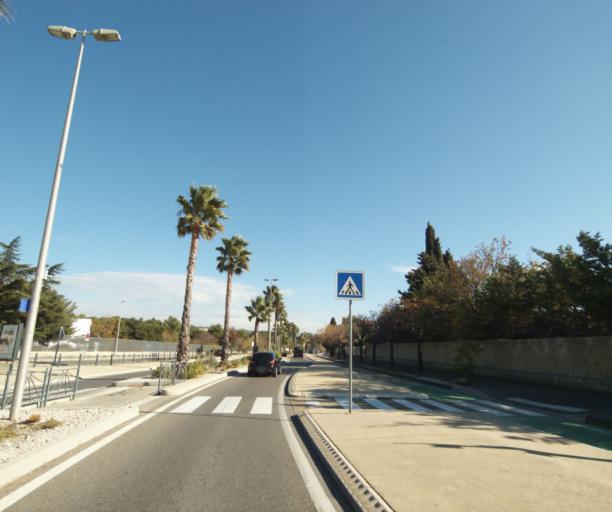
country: FR
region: Provence-Alpes-Cote d'Azur
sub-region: Departement des Bouches-du-Rhone
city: La Ciotat
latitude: 43.1925
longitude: 5.6129
